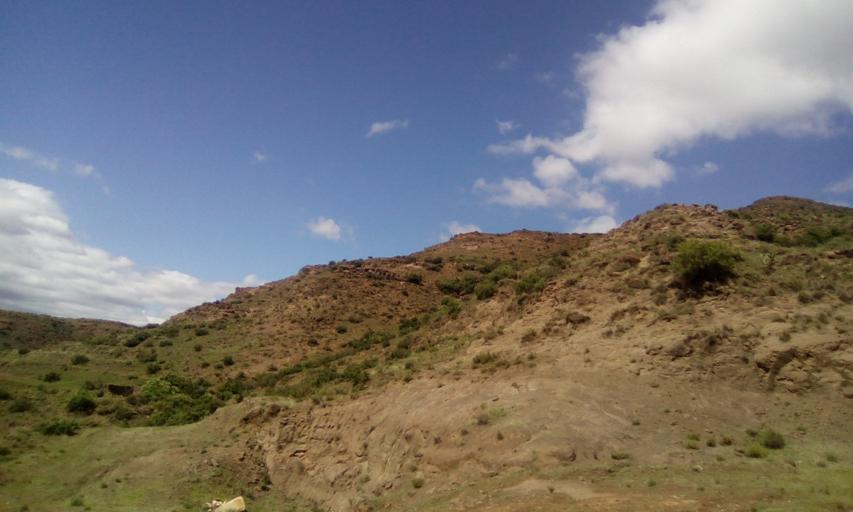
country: LS
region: Maseru
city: Nako
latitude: -29.6599
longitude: 27.7858
